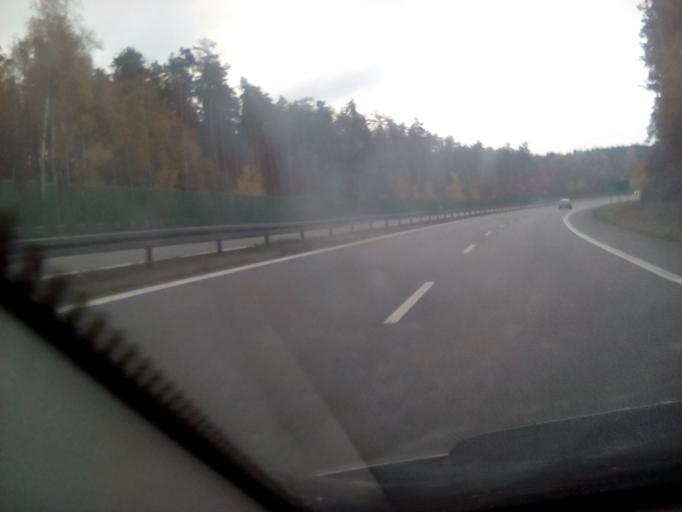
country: PL
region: Masovian Voivodeship
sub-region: Powiat bialobrzeski
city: Bialobrzegi
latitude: 51.6460
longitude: 20.9745
